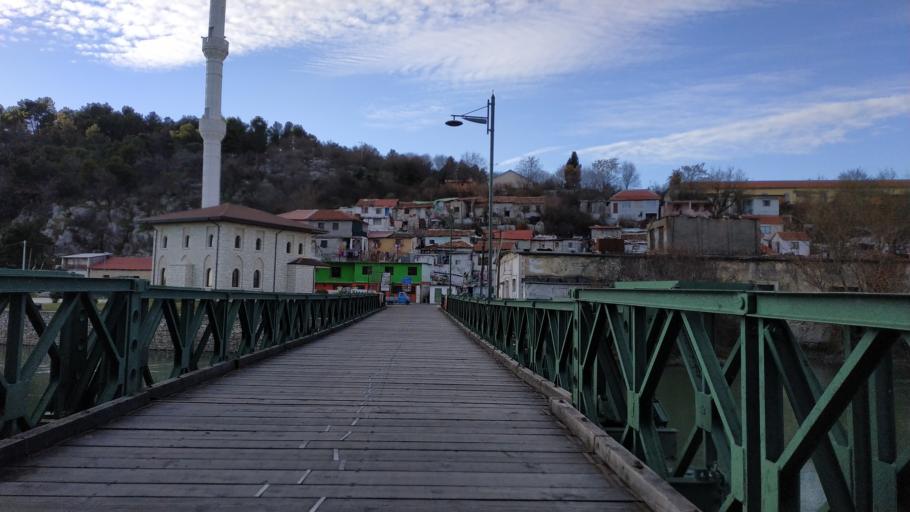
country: AL
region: Shkoder
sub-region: Rrethi i Shkodres
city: Shkoder
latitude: 42.0510
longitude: 19.4908
